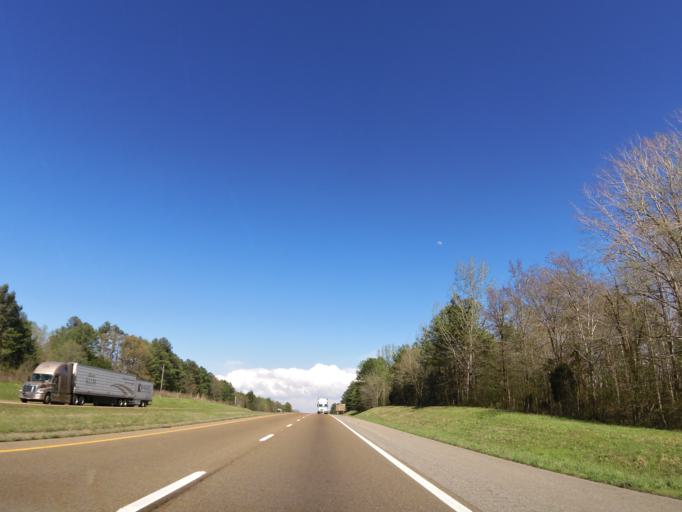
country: US
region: Tennessee
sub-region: Decatur County
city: Parsons
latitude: 35.8249
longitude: -88.1221
